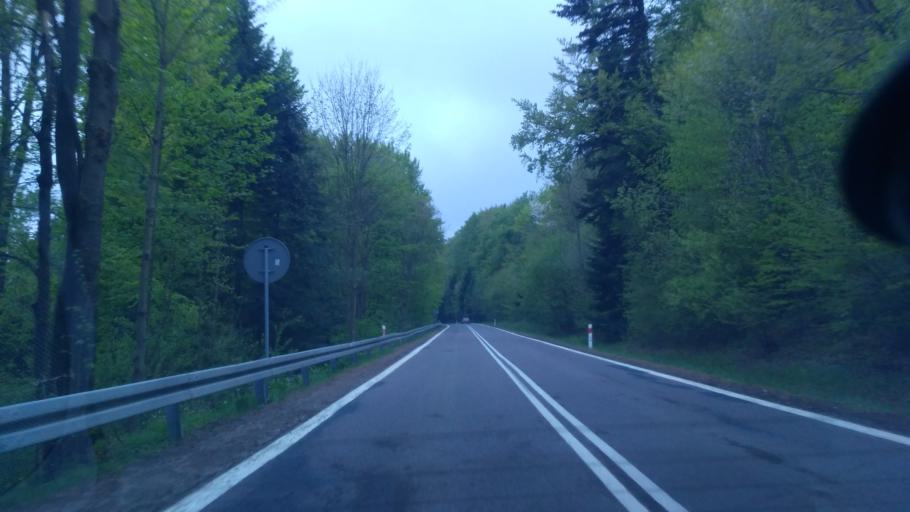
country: PL
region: Subcarpathian Voivodeship
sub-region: Powiat sanocki
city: Tyrawa Woloska
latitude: 49.5638
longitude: 22.3427
